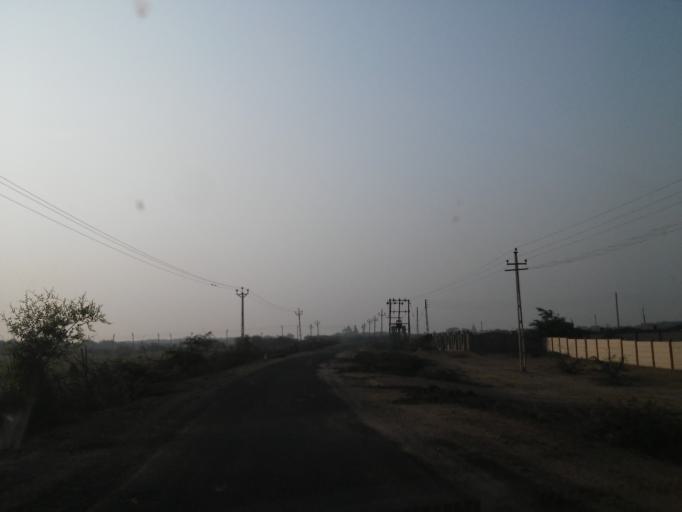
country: IN
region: Gujarat
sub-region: Kachchh
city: Mandvi
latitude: 22.8210
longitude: 69.3892
